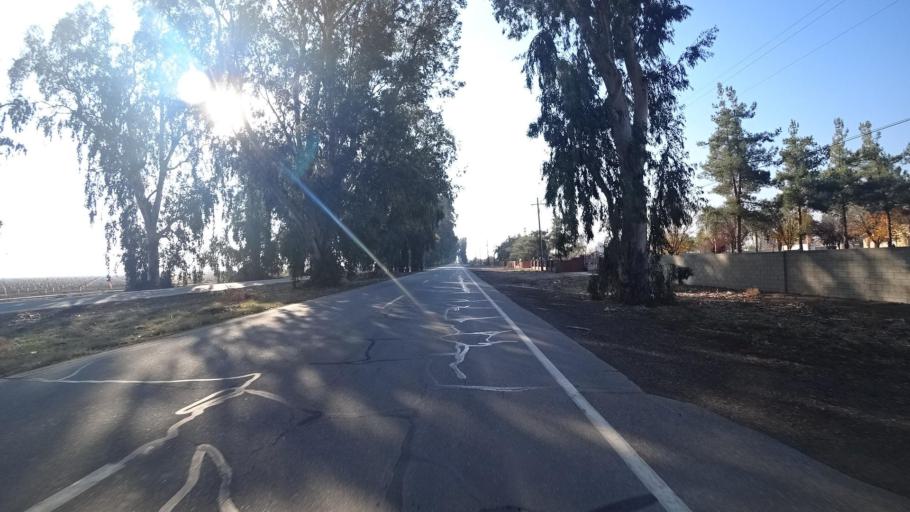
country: US
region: California
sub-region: Kern County
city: Greenfield
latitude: 35.1927
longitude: -119.0035
